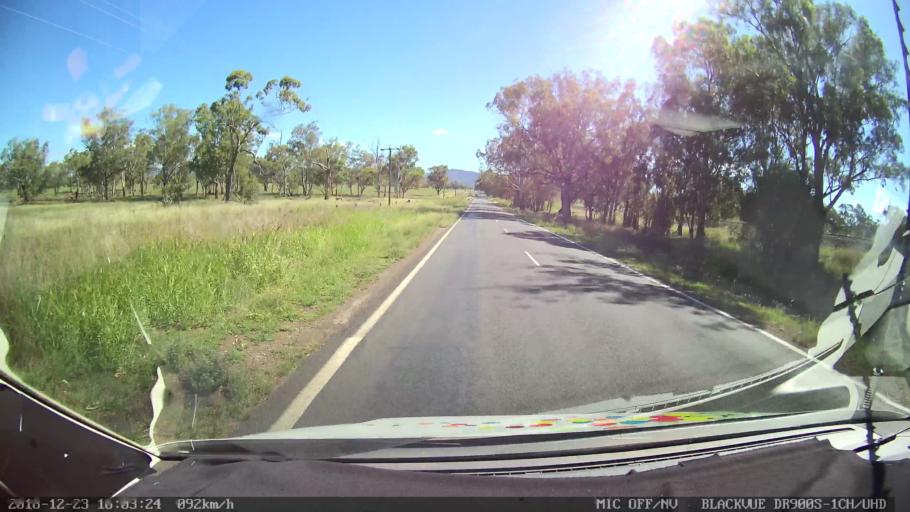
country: AU
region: New South Wales
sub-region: Tamworth Municipality
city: Phillip
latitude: -31.2430
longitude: 150.8010
